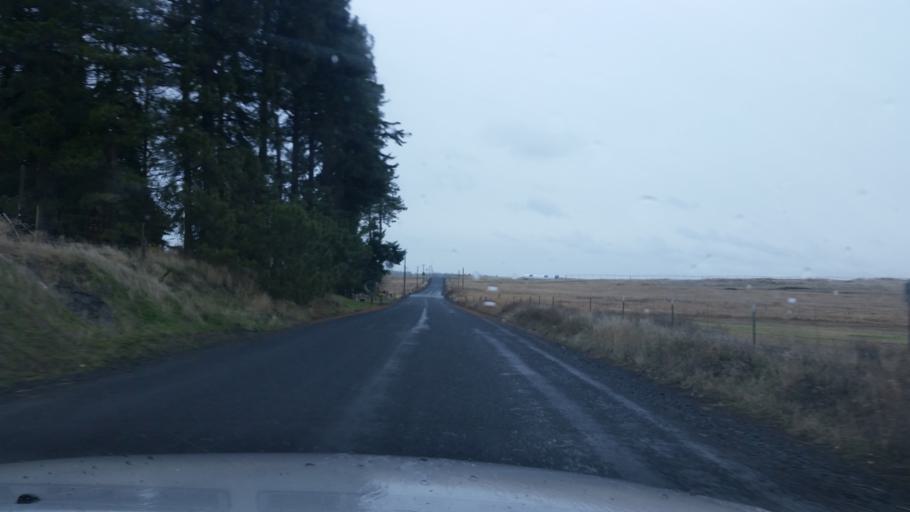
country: US
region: Washington
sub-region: Spokane County
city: Medical Lake
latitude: 47.6145
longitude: -117.7821
